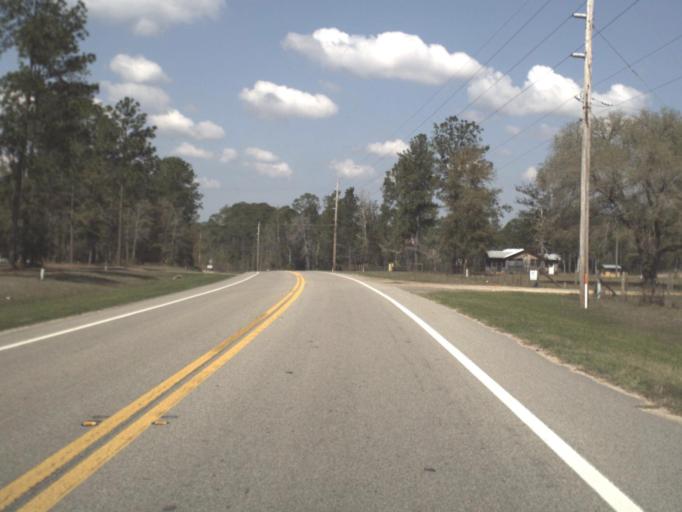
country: US
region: Florida
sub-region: Liberty County
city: Bristol
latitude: 30.4023
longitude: -84.8165
